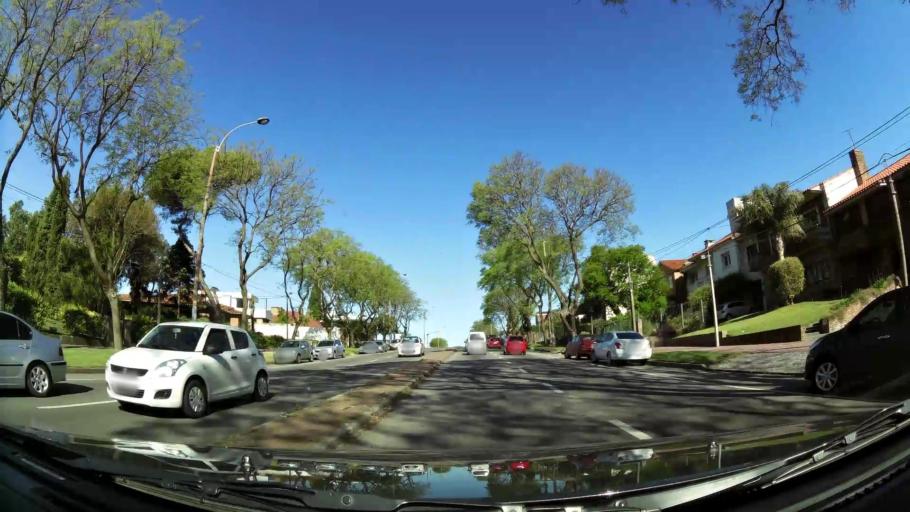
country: UY
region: Canelones
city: Paso de Carrasco
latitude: -34.8957
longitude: -56.0821
